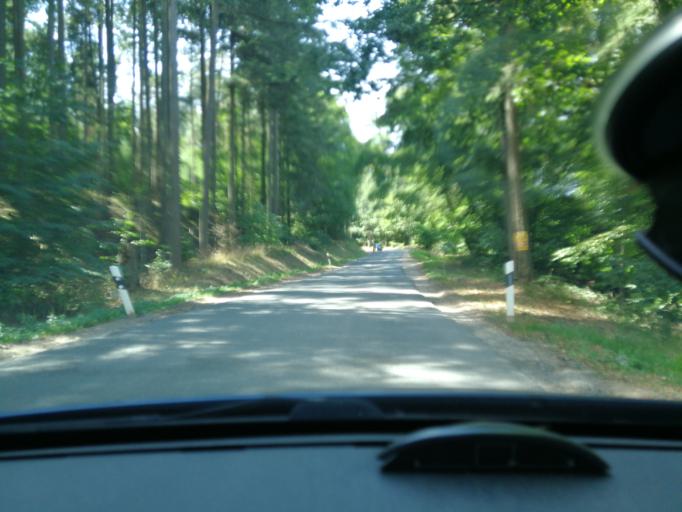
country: DE
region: Rheinland-Pfalz
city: Gladbach
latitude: 49.9225
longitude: 6.7695
